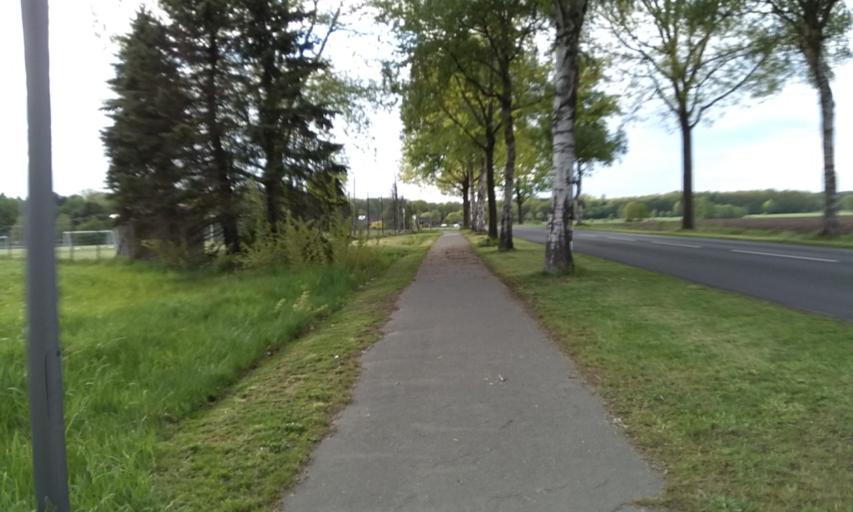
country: DE
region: Lower Saxony
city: Wohnste
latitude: 53.3874
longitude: 9.5442
